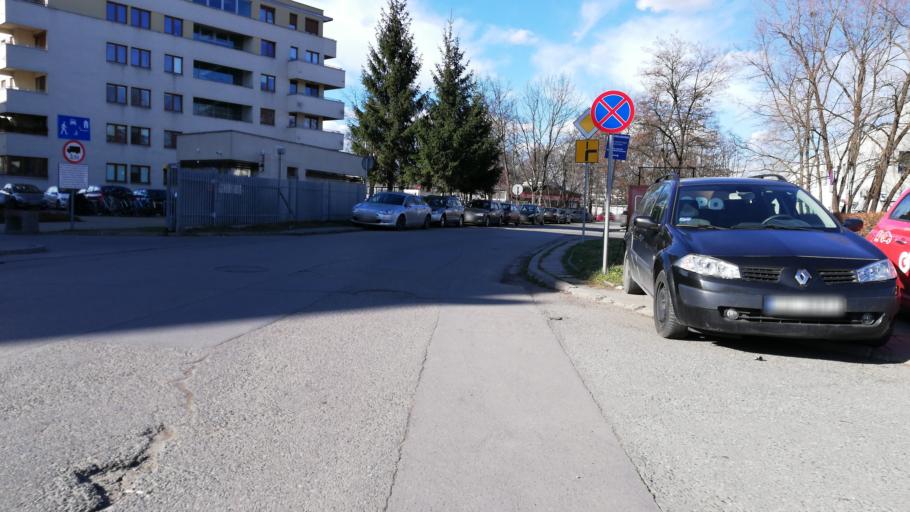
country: PL
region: Lesser Poland Voivodeship
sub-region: Krakow
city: Krakow
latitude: 50.0750
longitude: 19.9941
